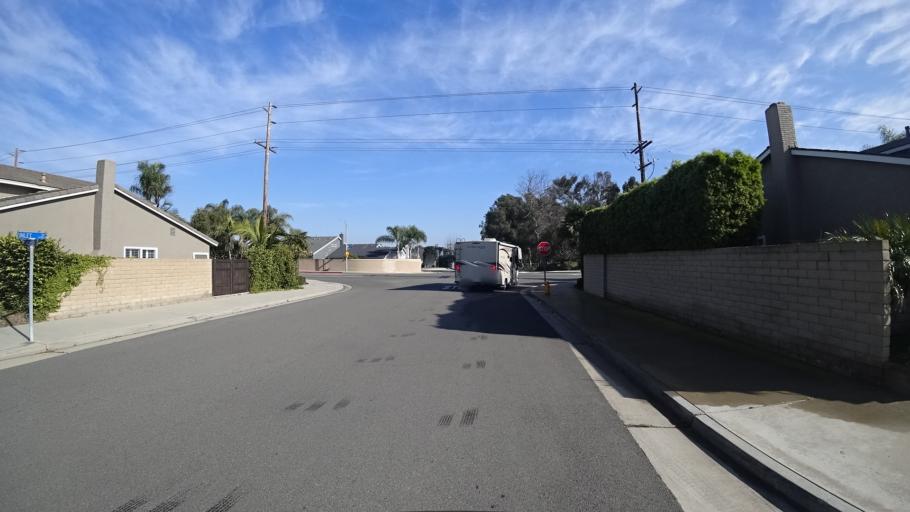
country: US
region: California
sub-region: Orange County
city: Huntington Beach
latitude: 33.6992
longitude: -118.0155
